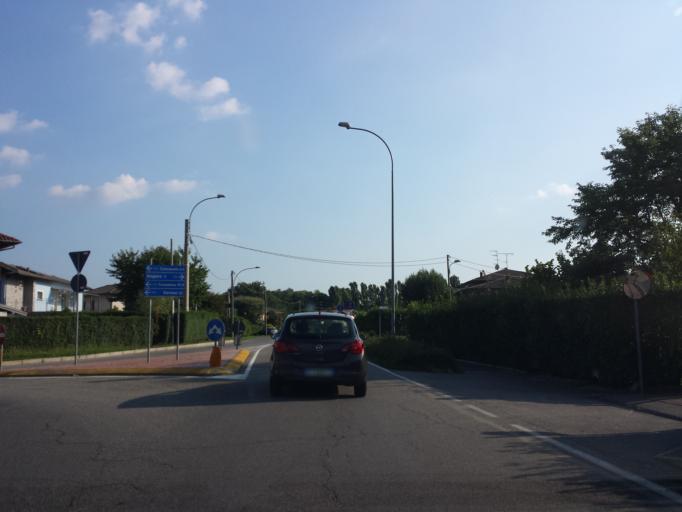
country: IT
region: Lombardy
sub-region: Provincia di Varese
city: Ispra
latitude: 45.8110
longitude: 8.6196
